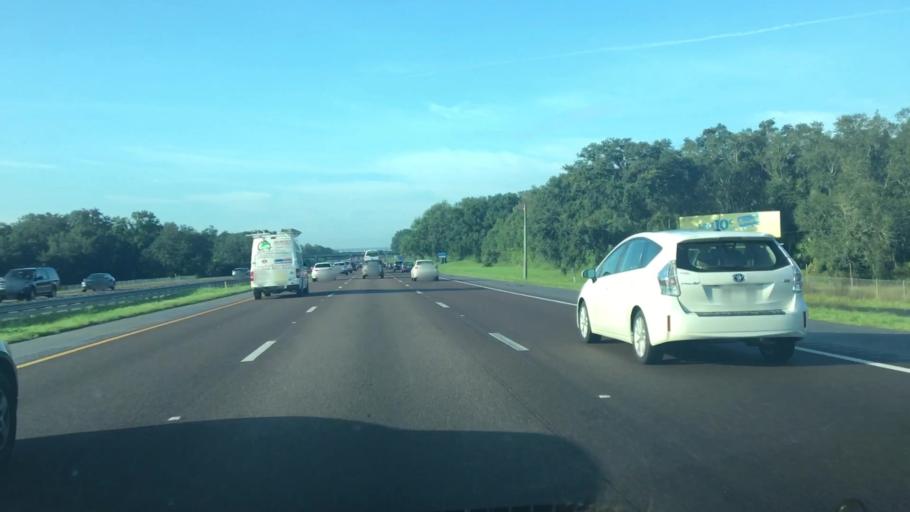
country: US
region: Florida
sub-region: Seminole County
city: Longwood
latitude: 28.7178
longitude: -81.3774
